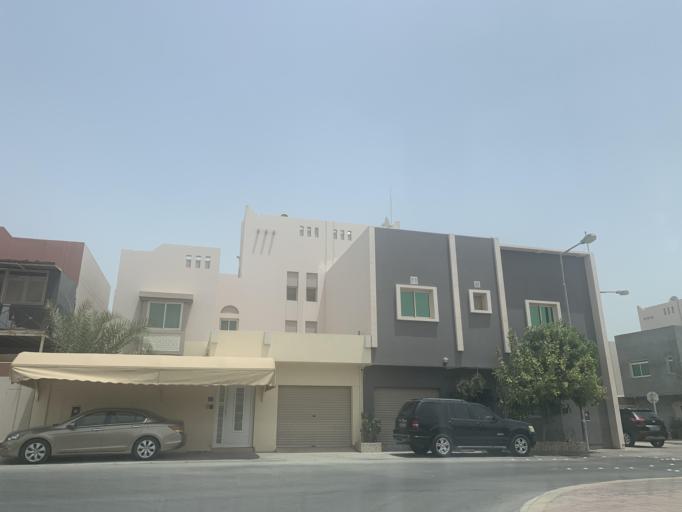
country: BH
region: Manama
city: Jidd Hafs
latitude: 26.2115
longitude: 50.5363
